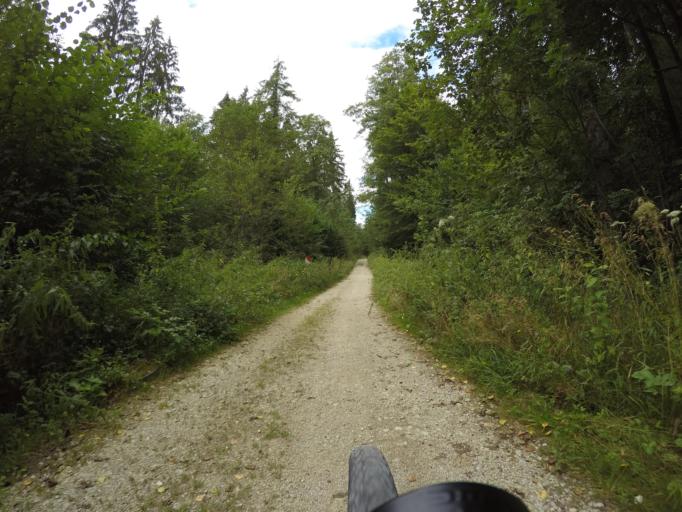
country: DE
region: Baden-Wuerttemberg
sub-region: Tuebingen Region
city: Reutlingen
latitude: 48.4542
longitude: 9.1719
